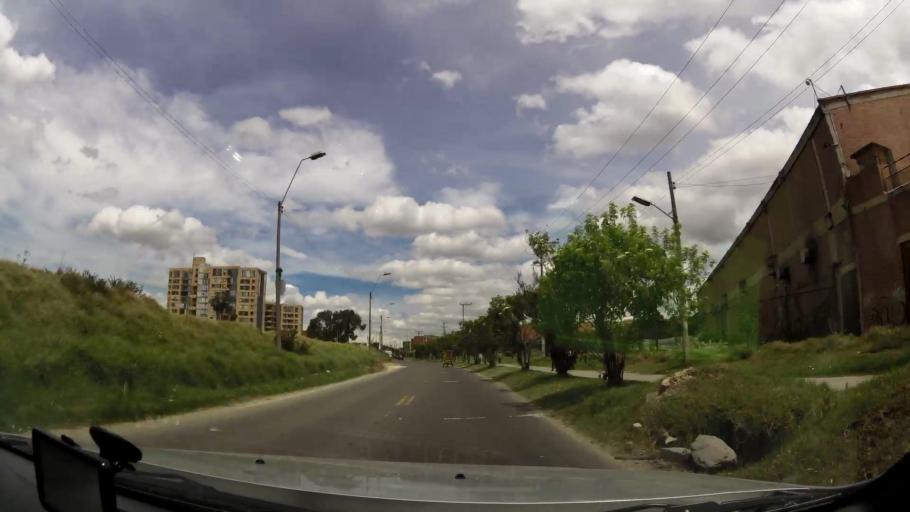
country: CO
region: Bogota D.C.
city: Bogota
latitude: 4.6475
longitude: -74.1335
